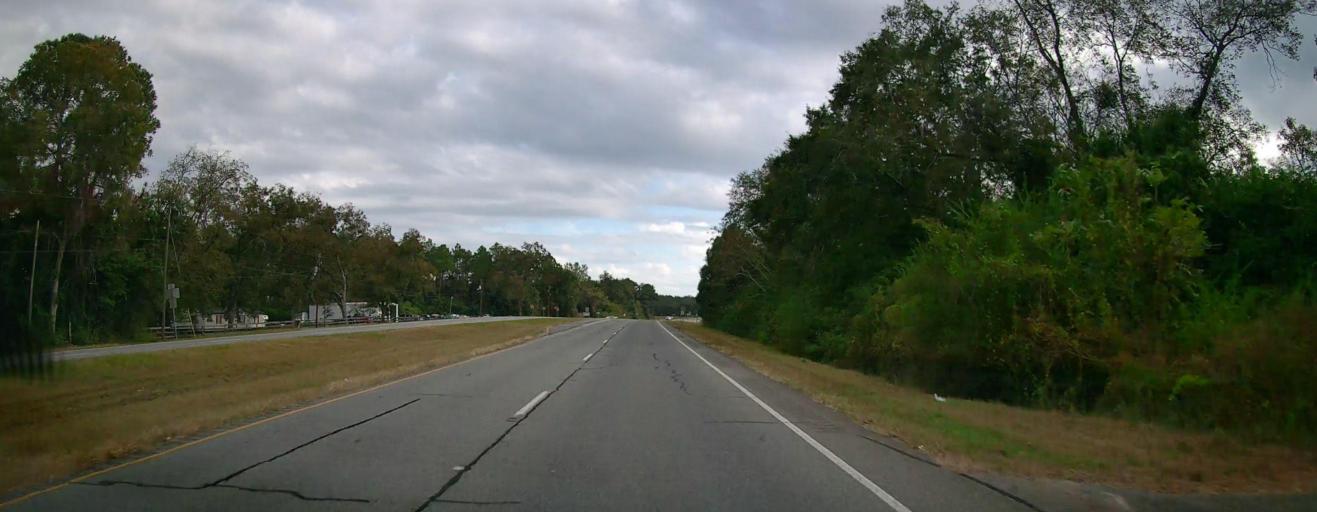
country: US
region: Georgia
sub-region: Thomas County
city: Meigs
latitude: 31.0801
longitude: -84.0824
